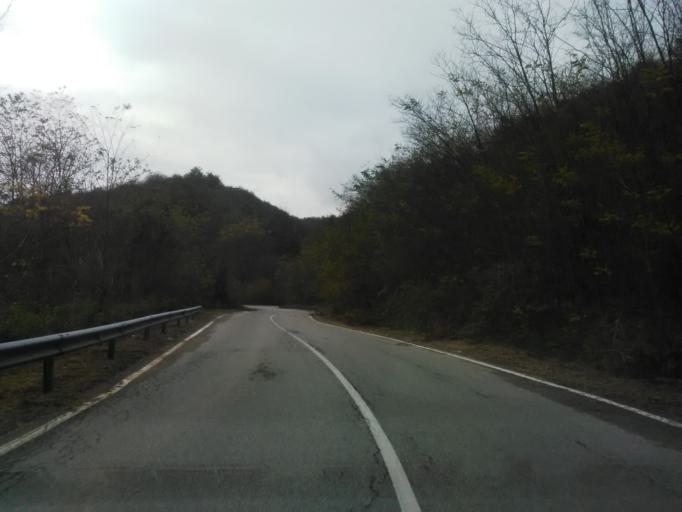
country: IT
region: Piedmont
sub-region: Provincia di Novara
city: Pogno
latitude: 45.7444
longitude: 8.3739
